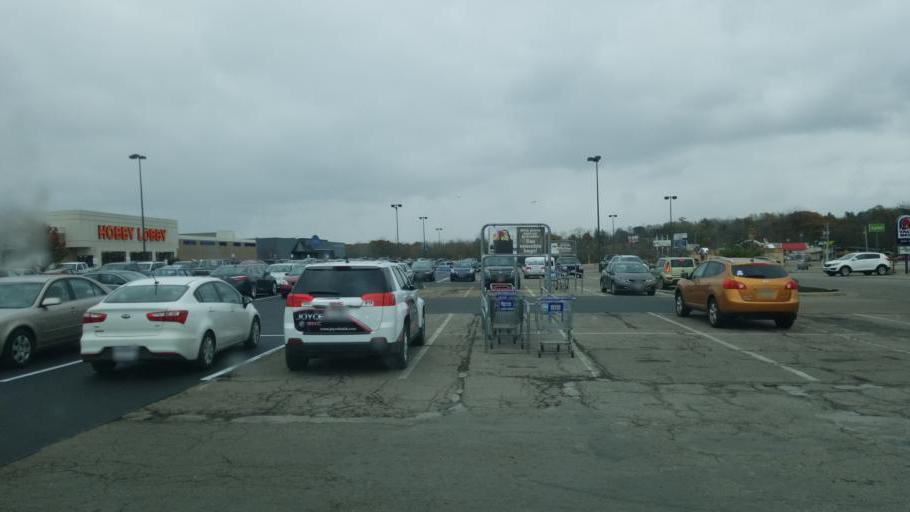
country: US
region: Ohio
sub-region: Richland County
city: Ontario
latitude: 40.7601
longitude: -82.5611
